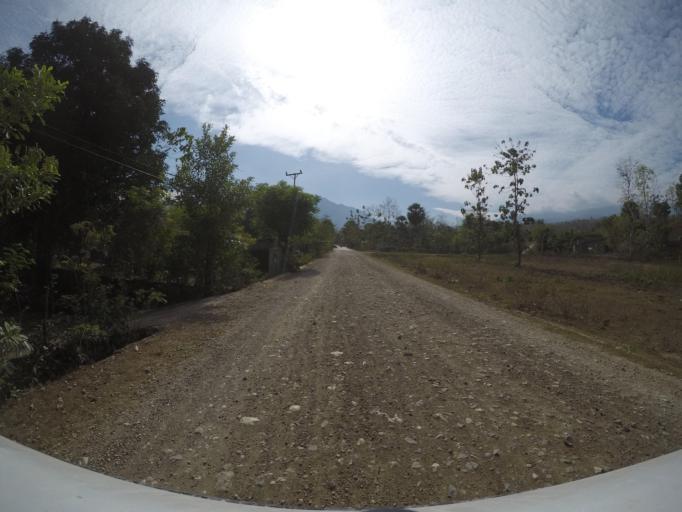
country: TL
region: Bobonaro
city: Maliana
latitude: -8.9935
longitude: 125.2080
